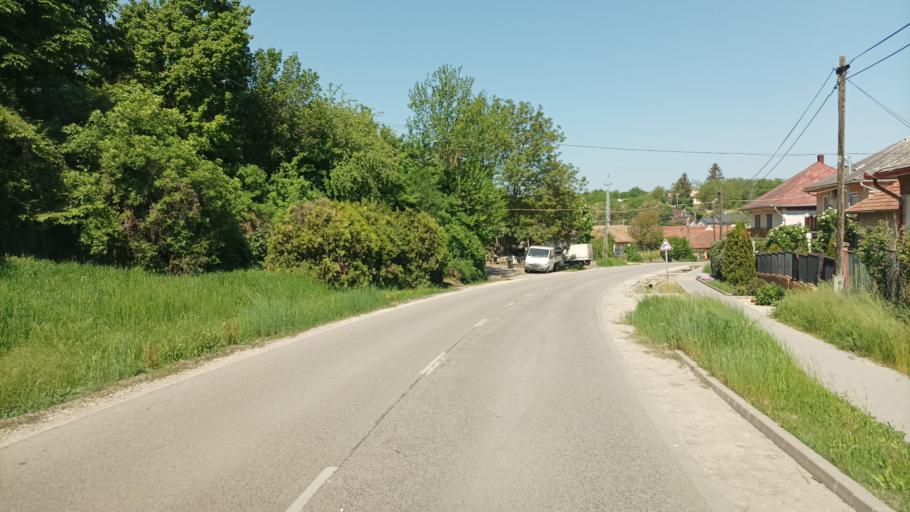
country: HU
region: Pest
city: Uri
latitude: 47.4135
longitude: 19.5200
